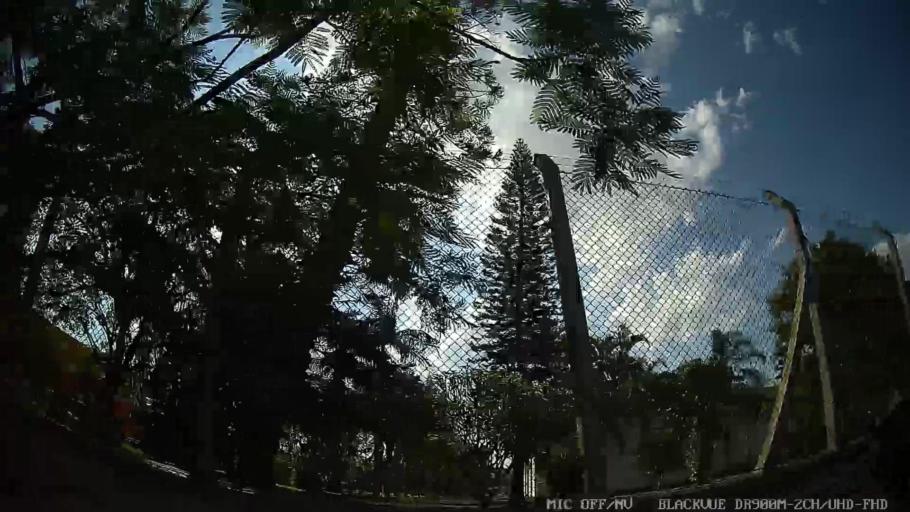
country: BR
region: Sao Paulo
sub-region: Ferraz De Vasconcelos
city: Ferraz de Vasconcelos
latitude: -23.5357
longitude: -46.4261
